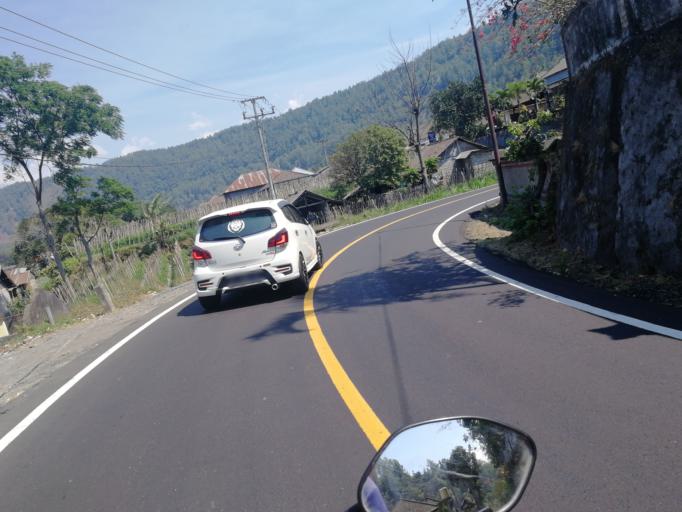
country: ID
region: Bali
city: Banjar Kedisan
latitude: -8.2773
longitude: 115.3790
